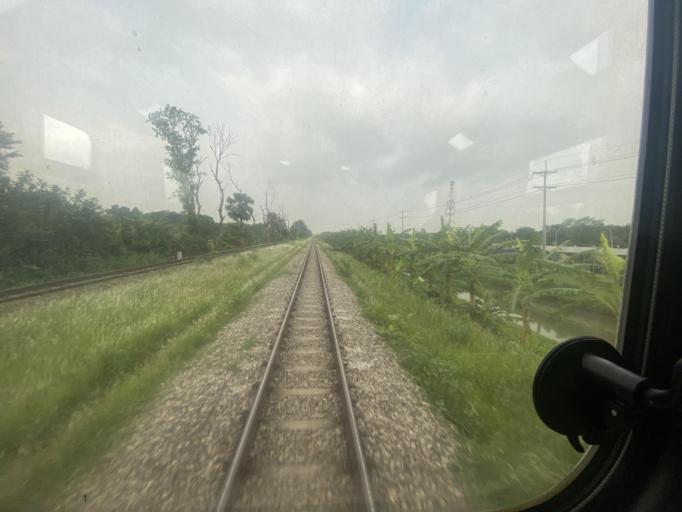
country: BD
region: Dhaka
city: Tungi
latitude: 23.9325
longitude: 90.5188
